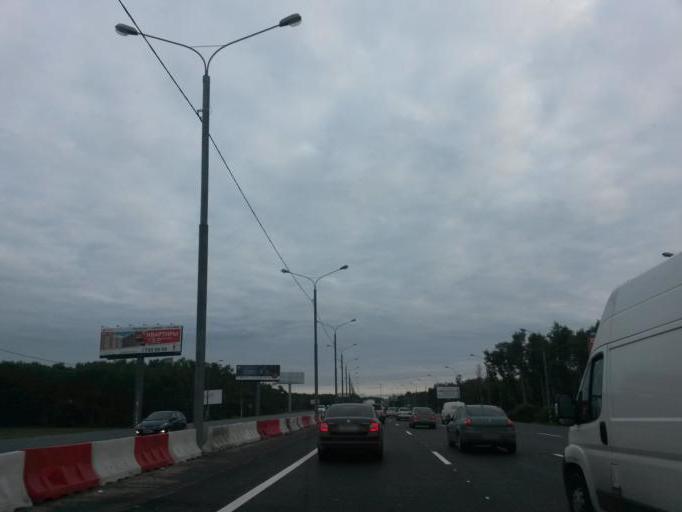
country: RU
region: Moscow
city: Annino
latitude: 55.5388
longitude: 37.6095
